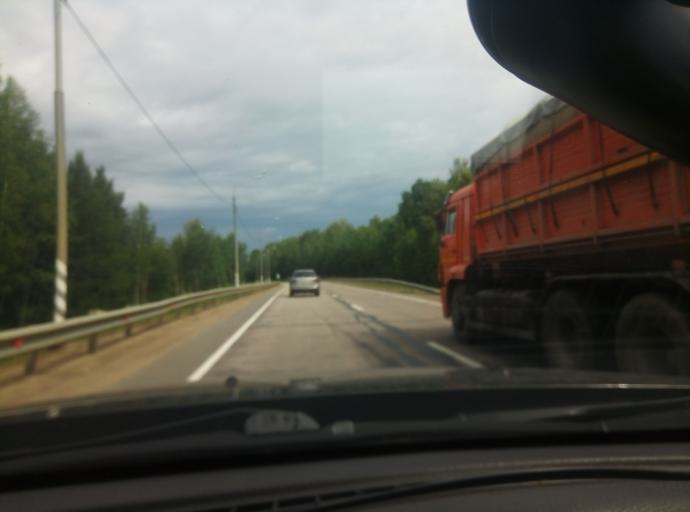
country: RU
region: Tula
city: Leninskiy
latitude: 54.4089
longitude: 37.5020
